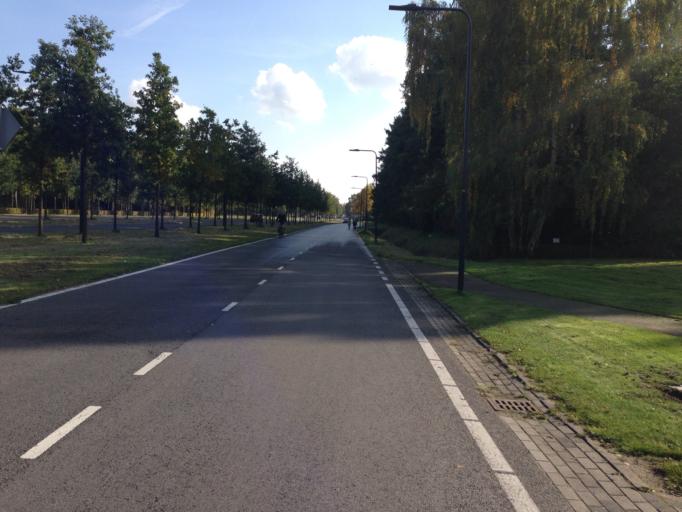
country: NL
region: Overijssel
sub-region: Gemeente Enschede
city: Enschede
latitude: 52.2356
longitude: 6.8558
